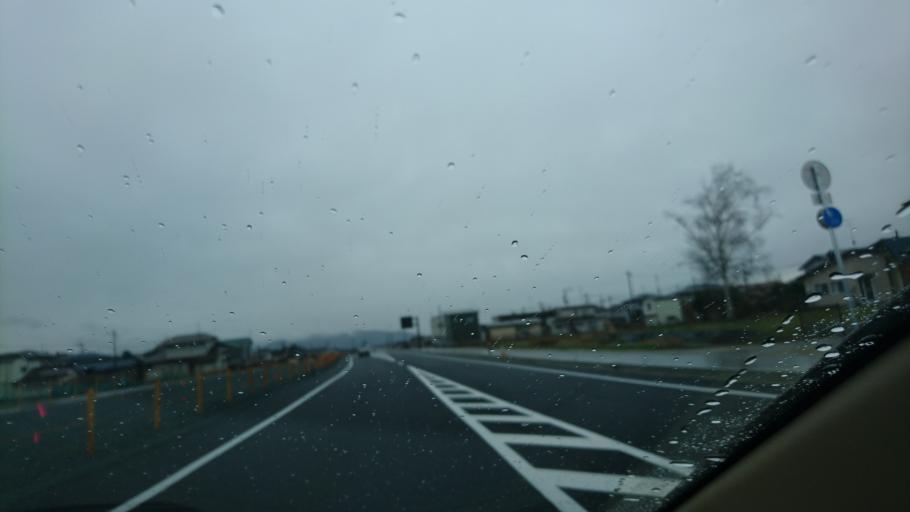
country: JP
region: Iwate
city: Mizusawa
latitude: 39.1341
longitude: 141.1624
